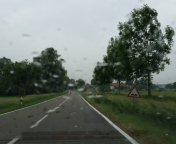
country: DE
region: Bavaria
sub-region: Upper Bavaria
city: Rohrenfels
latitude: 48.6843
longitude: 11.1507
